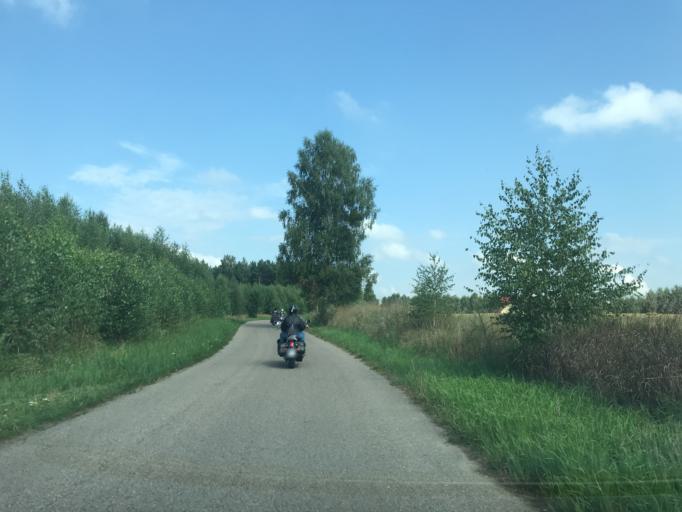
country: PL
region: Warmian-Masurian Voivodeship
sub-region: Powiat nowomiejski
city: Biskupiec
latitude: 53.4291
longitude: 19.4388
